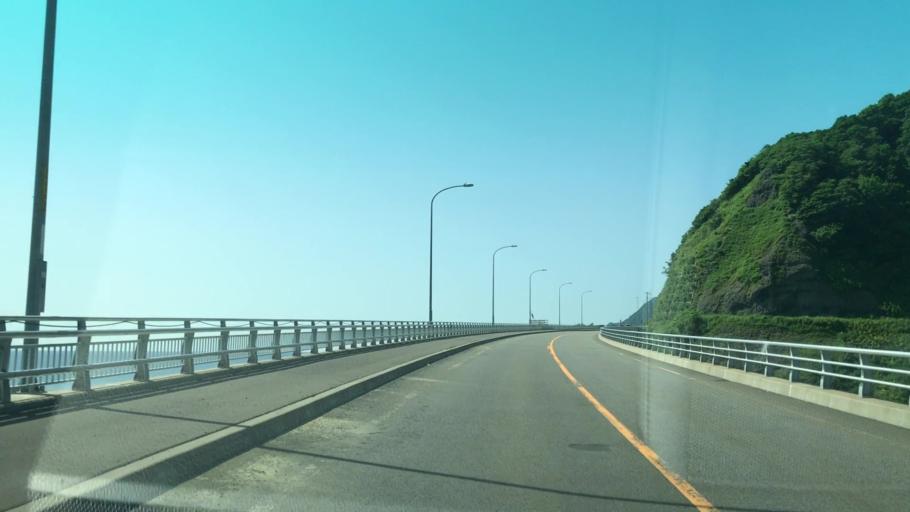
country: JP
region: Hokkaido
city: Iwanai
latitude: 43.1299
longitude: 140.4372
